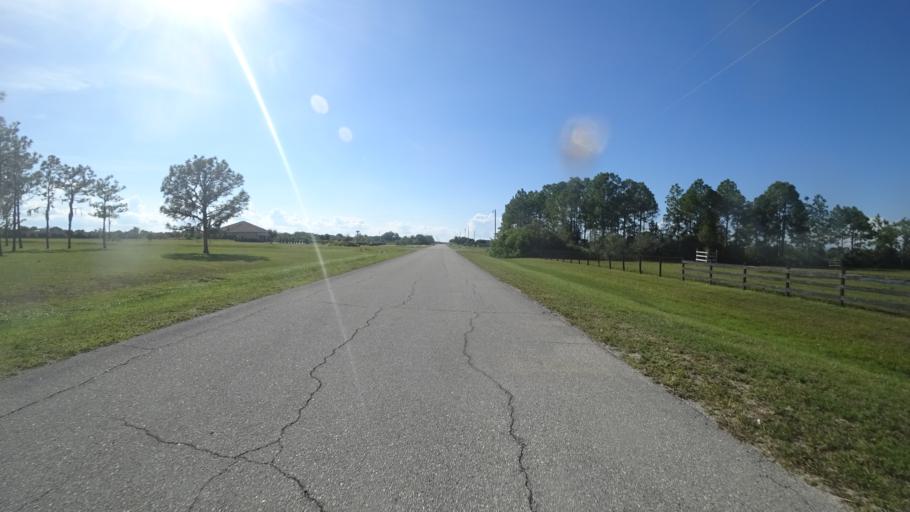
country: US
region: Florida
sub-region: Sarasota County
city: The Meadows
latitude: 27.4232
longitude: -82.2781
